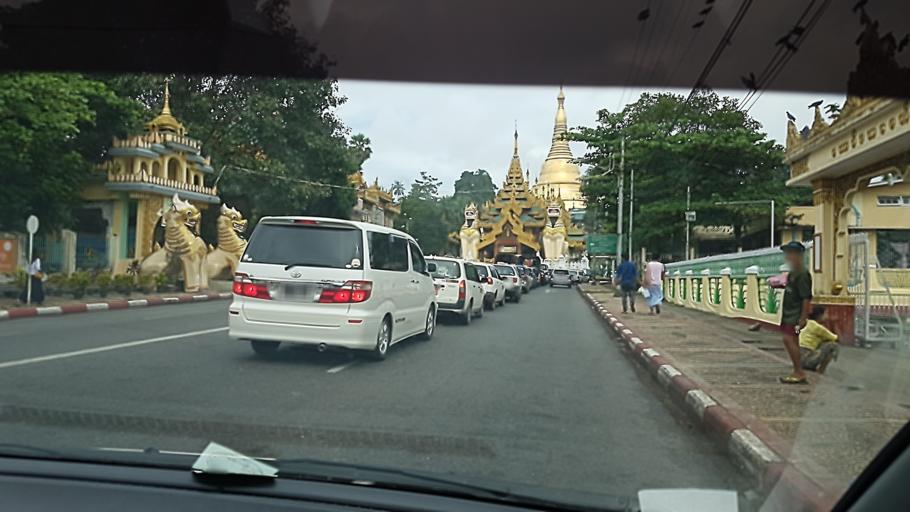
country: MM
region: Yangon
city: Yangon
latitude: 16.7946
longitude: 96.1508
